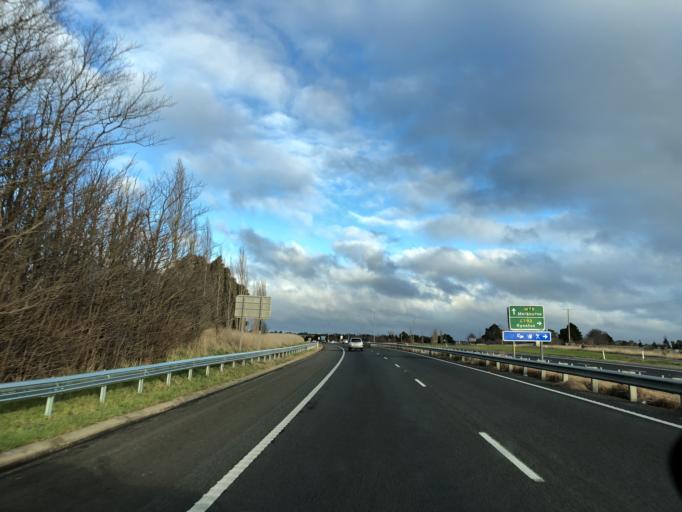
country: AU
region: Victoria
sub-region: Mount Alexander
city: Castlemaine
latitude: -37.2174
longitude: 144.4153
